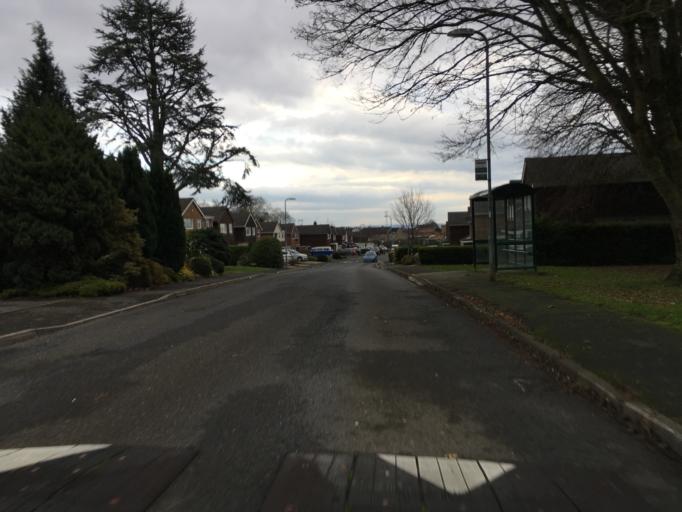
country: GB
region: Wales
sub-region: Monmouthshire
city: Chepstow
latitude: 51.6320
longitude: -2.6832
